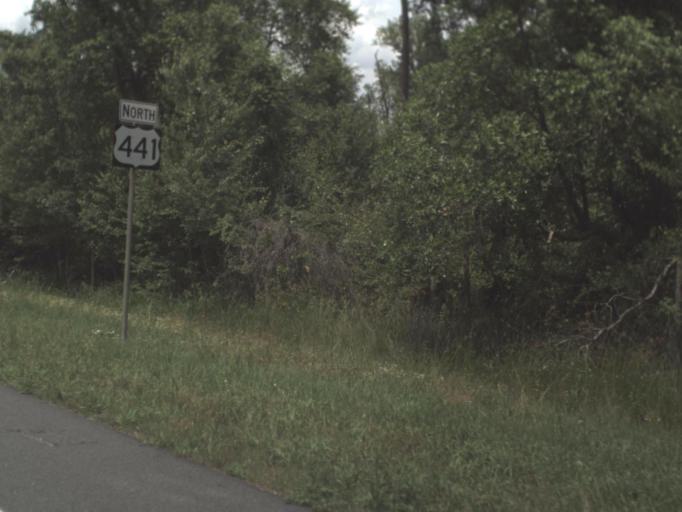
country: US
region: Florida
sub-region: Hamilton County
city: Jasper
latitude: 30.5197
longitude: -82.6720
